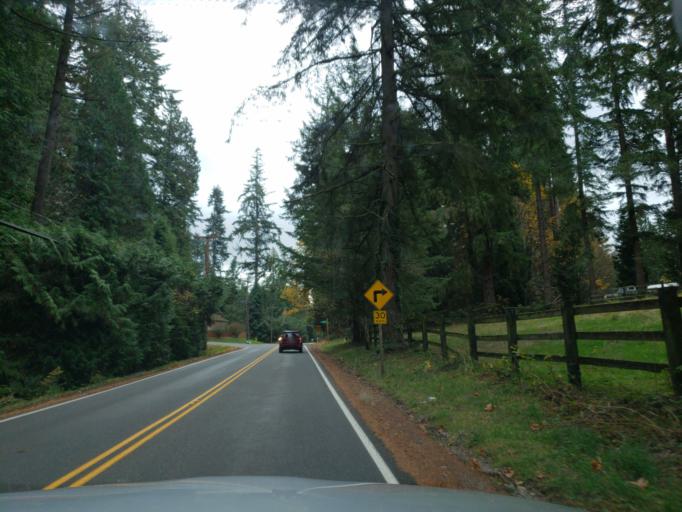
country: US
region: Washington
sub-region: King County
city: Woodinville
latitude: 47.7479
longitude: -122.1300
